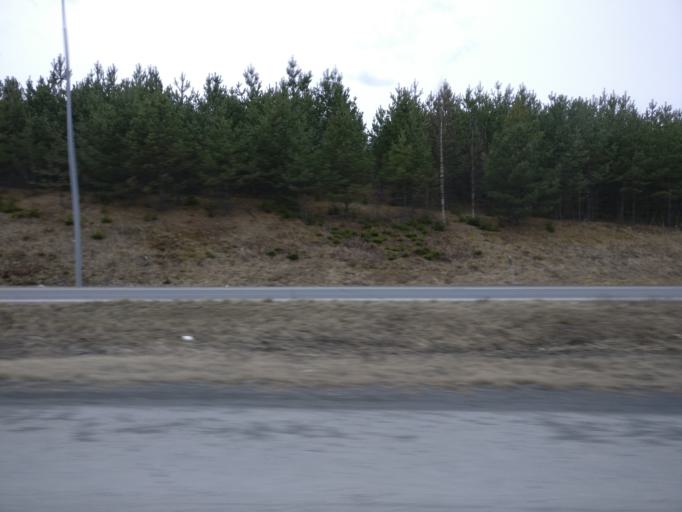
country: FI
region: Pirkanmaa
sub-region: Etelae-Pirkanmaa
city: Viiala
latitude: 61.2558
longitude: 23.8356
